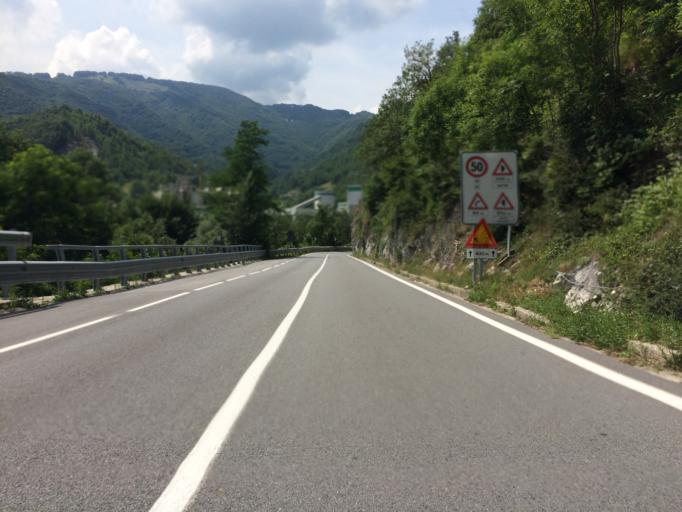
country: IT
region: Piedmont
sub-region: Provincia di Cuneo
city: Vernante
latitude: 44.2607
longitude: 7.5210
